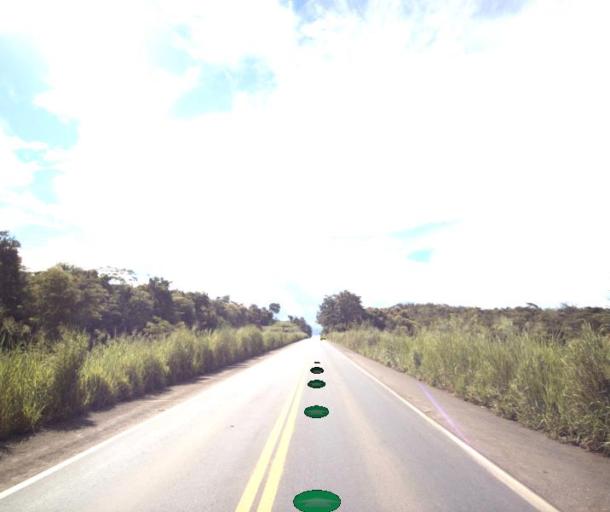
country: BR
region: Goias
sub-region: Jaragua
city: Jaragua
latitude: -15.7989
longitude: -49.3003
